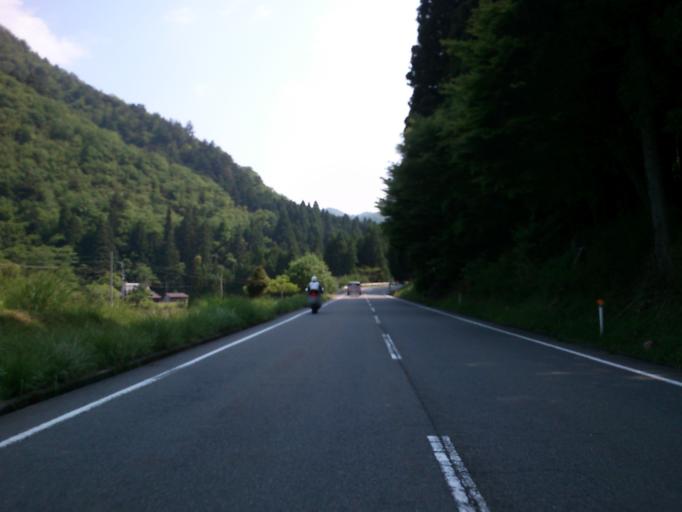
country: JP
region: Kyoto
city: Kameoka
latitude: 35.2503
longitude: 135.5614
